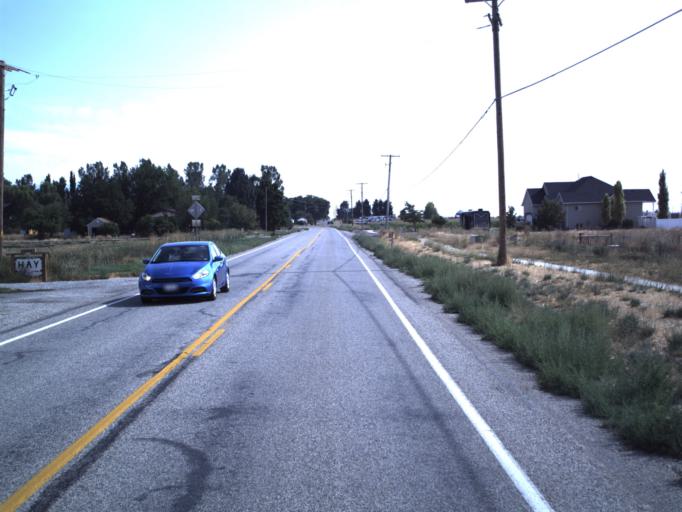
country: US
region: Utah
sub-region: Box Elder County
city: Honeyville
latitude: 41.6496
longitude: -112.0849
